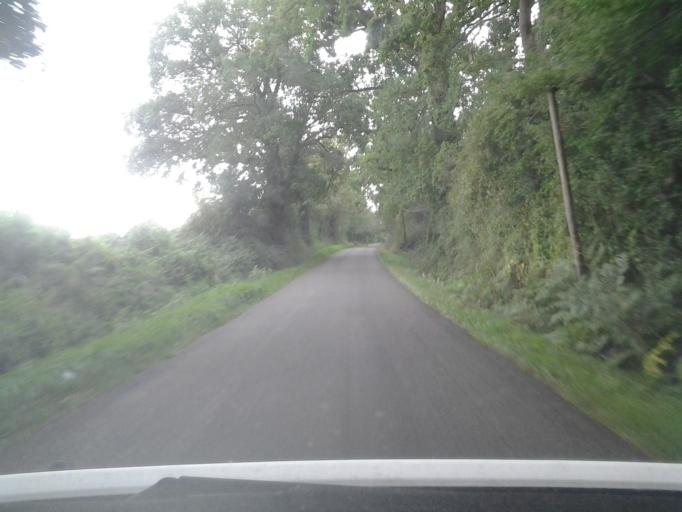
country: FR
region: Pays de la Loire
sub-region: Departement de la Vendee
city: La Roche-sur-Yon
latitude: 46.6928
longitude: -1.4042
